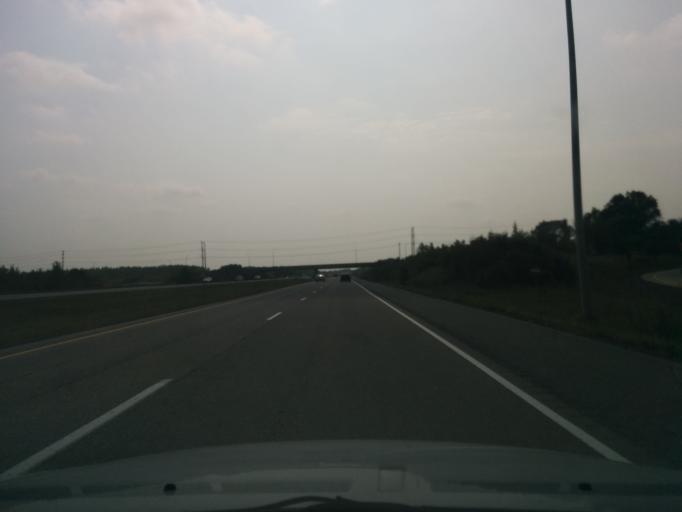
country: CA
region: Ontario
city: Bells Corners
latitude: 45.2738
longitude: -75.7985
